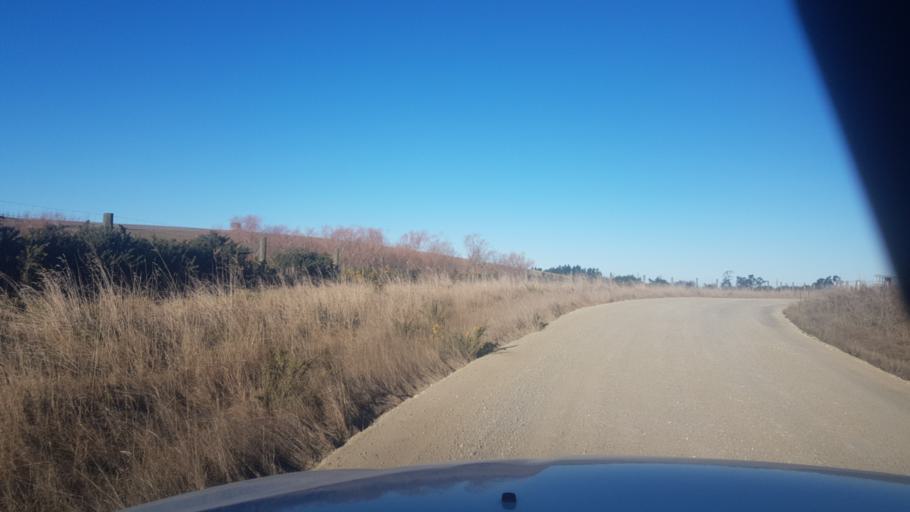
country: NZ
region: Canterbury
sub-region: Timaru District
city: Pleasant Point
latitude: -44.3655
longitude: 171.0714
